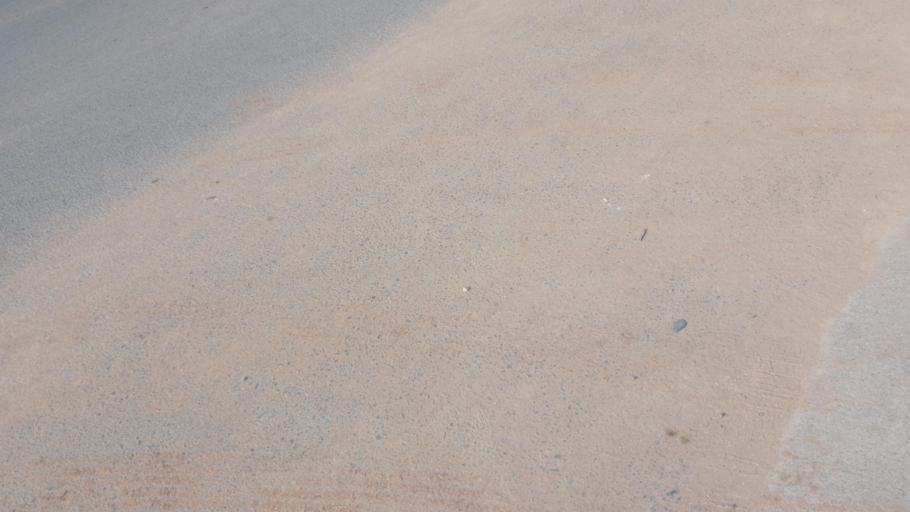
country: ZM
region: Lusaka
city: Lusaka
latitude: -15.3988
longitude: 28.3880
